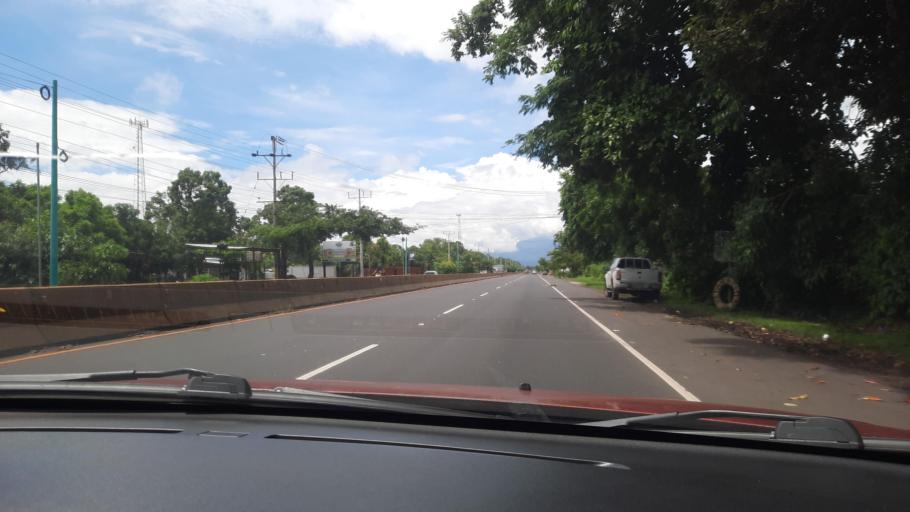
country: SV
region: Sonsonate
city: Acajutla
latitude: 13.6301
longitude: -89.7842
